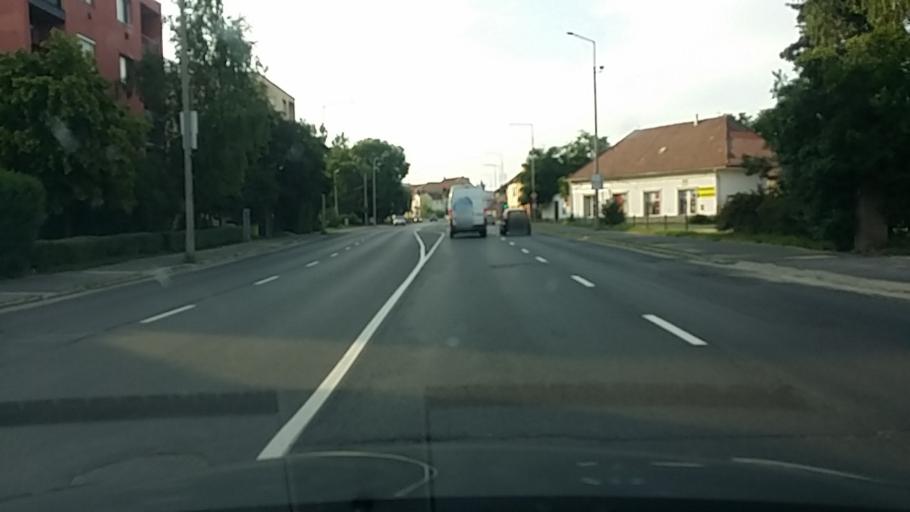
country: HU
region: Borsod-Abauj-Zemplen
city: Miskolc
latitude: 48.0708
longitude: 20.7901
